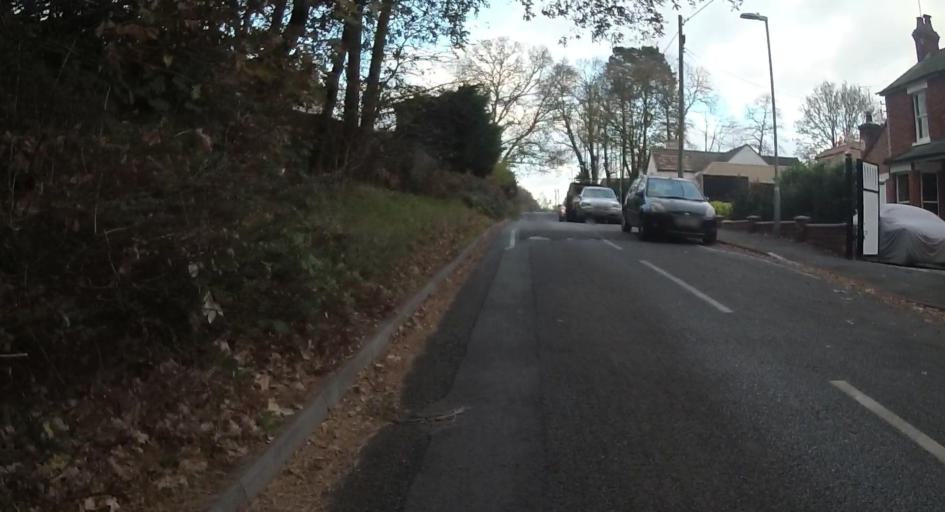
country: GB
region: England
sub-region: Bracknell Forest
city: Sandhurst
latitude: 51.3568
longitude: -0.7808
